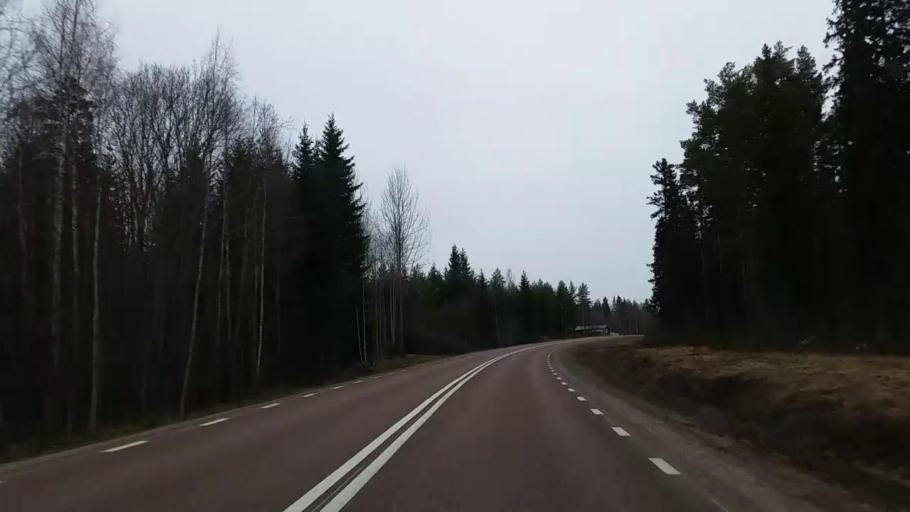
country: SE
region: Gaevleborg
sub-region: Ovanakers Kommun
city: Edsbyn
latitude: 61.2550
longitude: 15.8856
